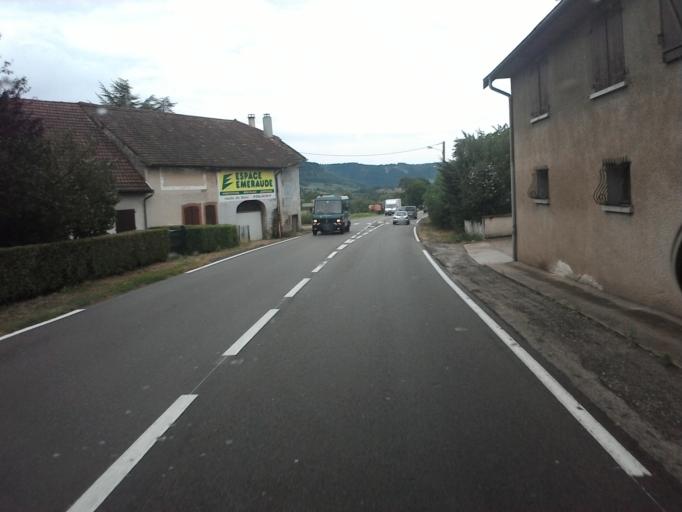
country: FR
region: Franche-Comte
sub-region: Departement du Jura
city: Poligny
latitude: 46.8680
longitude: 5.7164
